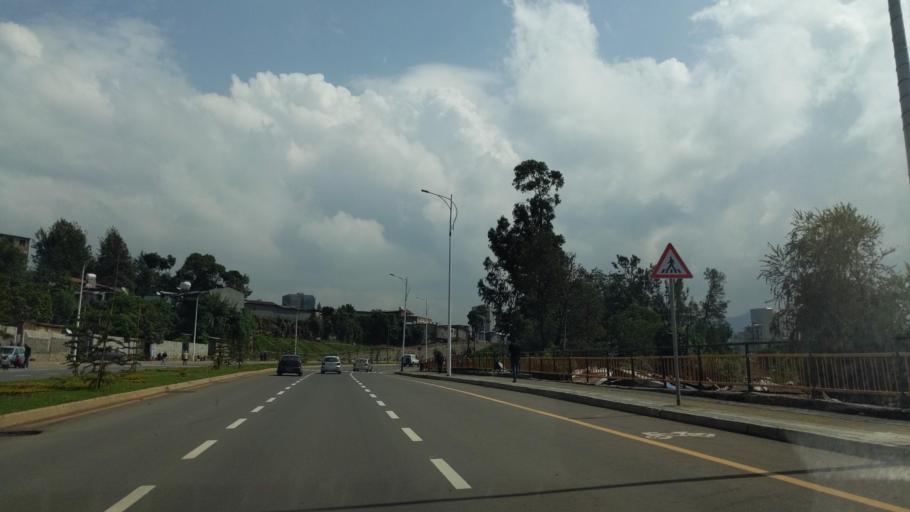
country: ET
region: Adis Abeba
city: Addis Ababa
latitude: 9.0037
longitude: 38.7736
